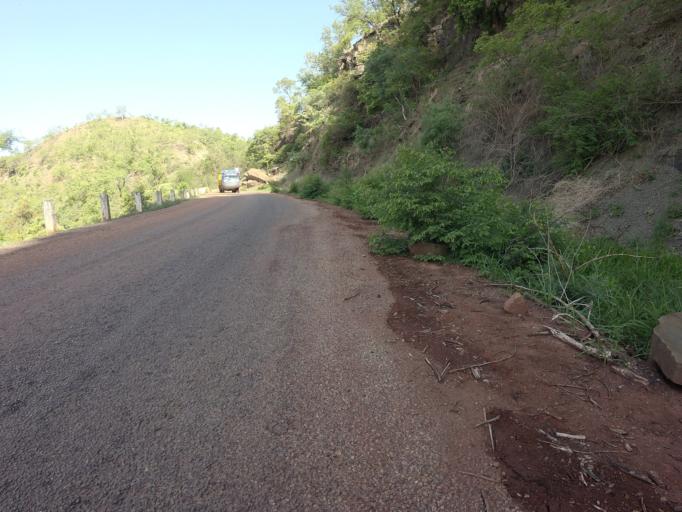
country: GH
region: Upper East
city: Bawku
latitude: 10.6423
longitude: -0.1958
